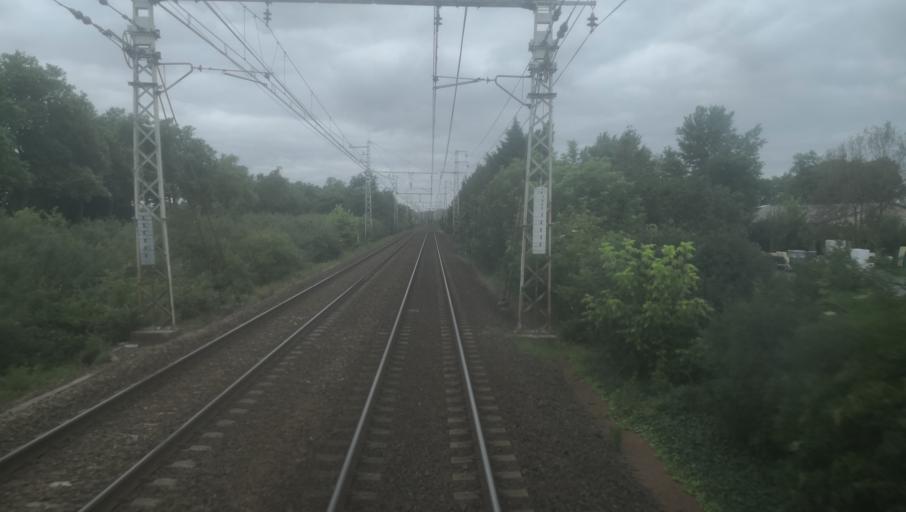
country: FR
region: Midi-Pyrenees
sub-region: Departement de la Haute-Garonne
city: Saint-Jory
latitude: 43.7276
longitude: 1.3782
